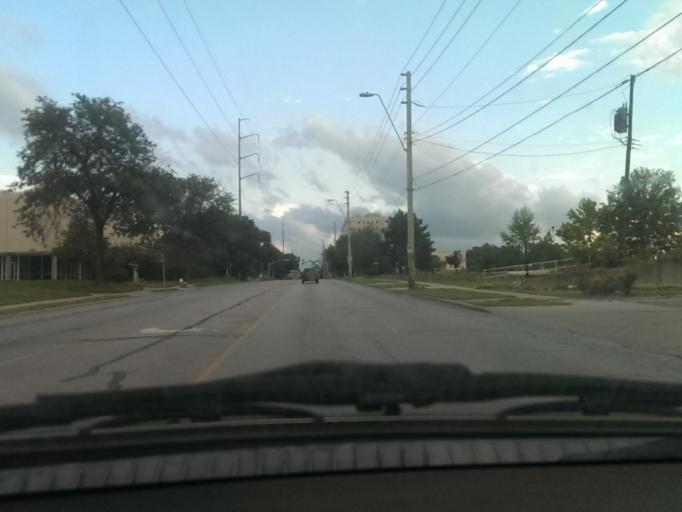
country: US
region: Kansas
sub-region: Johnson County
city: Mission Hills
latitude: 39.0083
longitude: -94.5749
